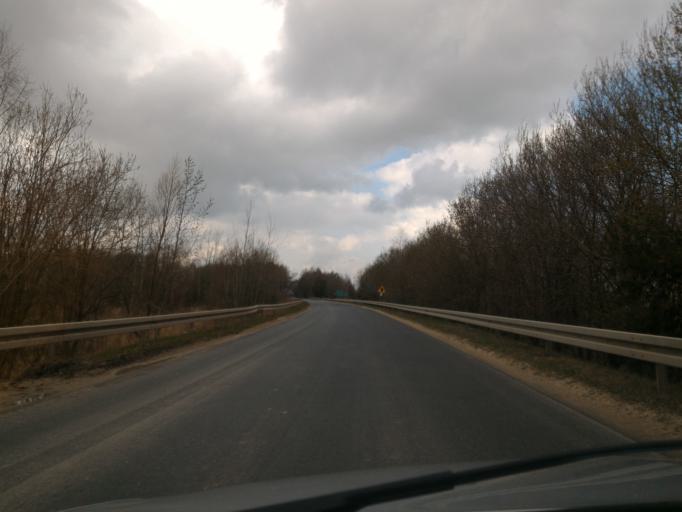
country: CZ
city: Hradek nad Nisou
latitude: 50.8849
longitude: 14.8809
